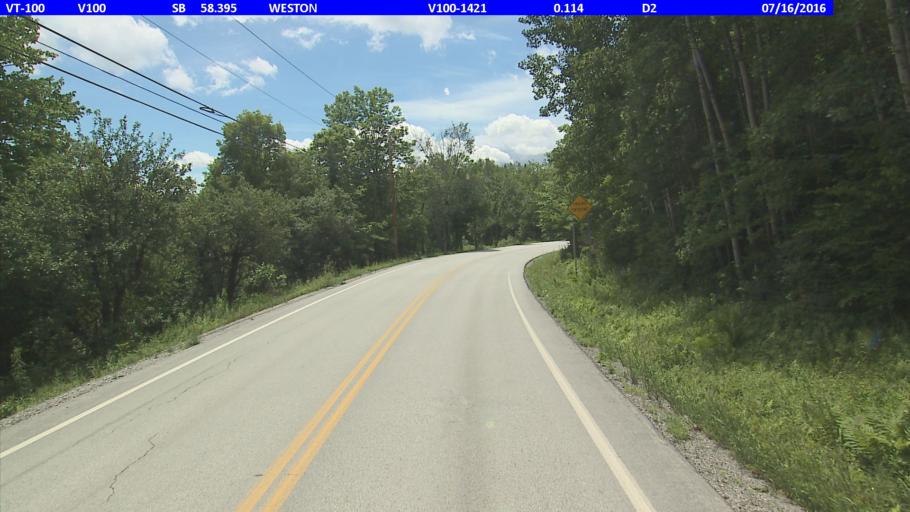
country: US
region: Vermont
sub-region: Windsor County
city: Chester
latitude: 43.2513
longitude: -72.7952
